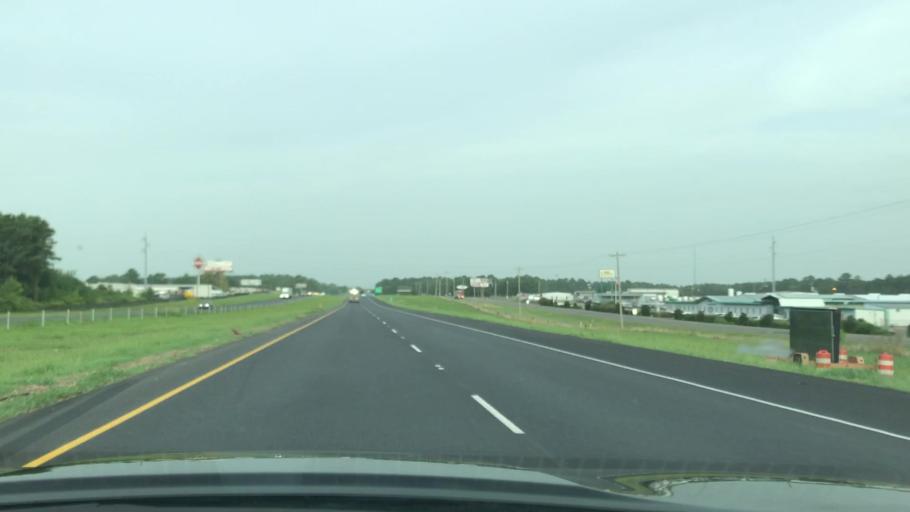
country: US
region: Louisiana
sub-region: Caddo Parish
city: Greenwood
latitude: 32.4454
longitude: -93.9209
